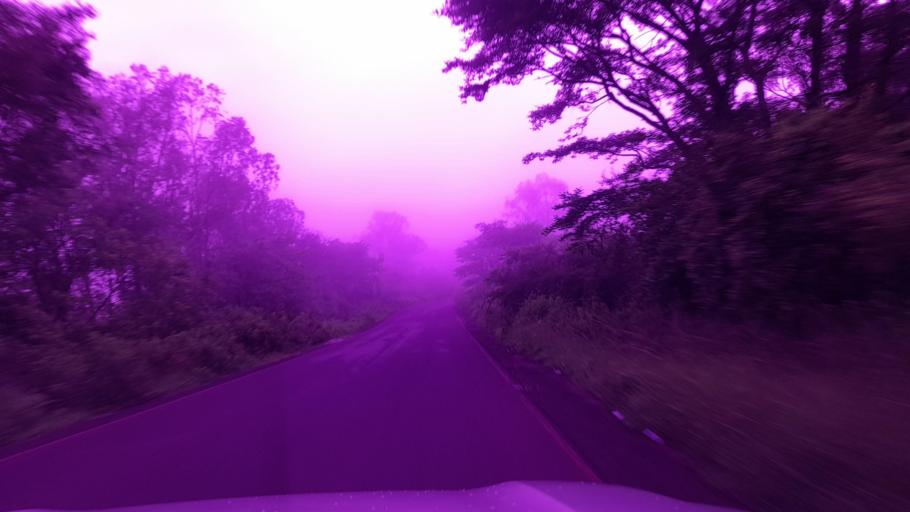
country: ET
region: Oromiya
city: Waliso
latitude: 8.1726
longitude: 37.5524
